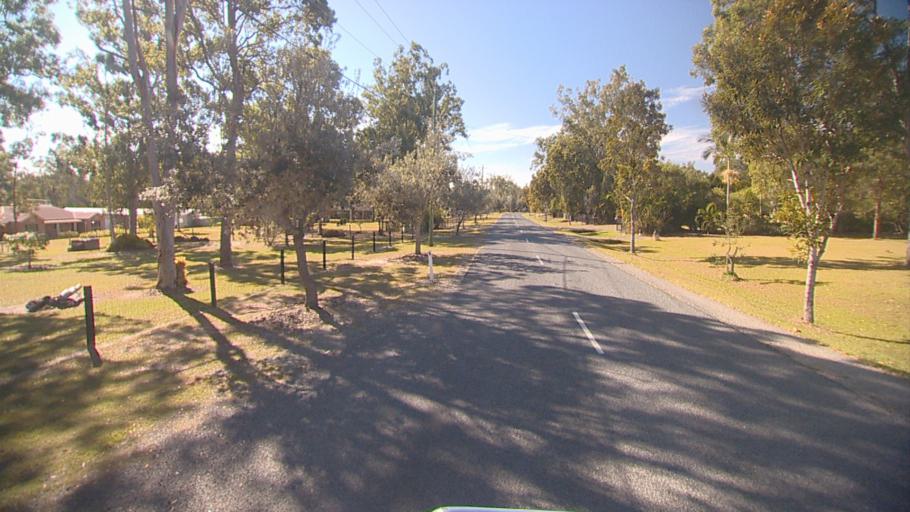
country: AU
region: Queensland
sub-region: Logan
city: North Maclean
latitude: -27.7437
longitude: 152.9548
